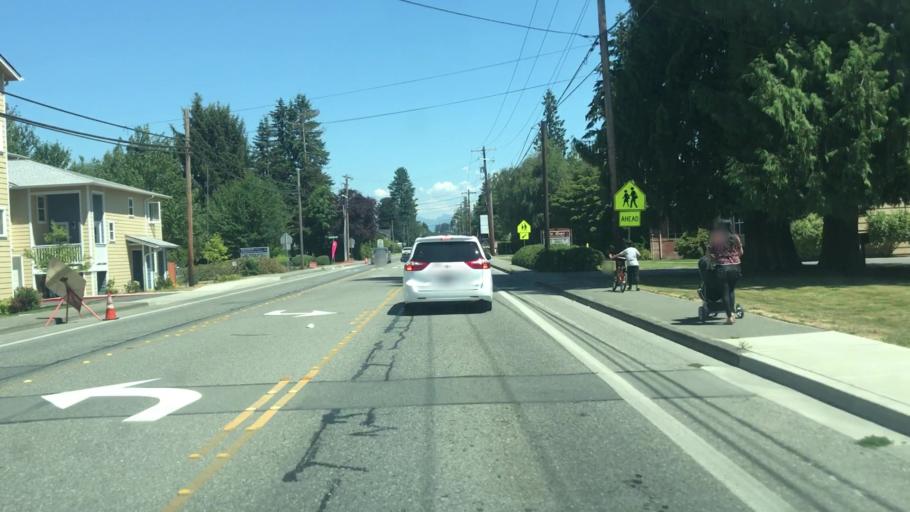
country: US
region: Washington
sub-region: Snohomish County
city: Monroe
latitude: 47.8512
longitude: -121.9852
